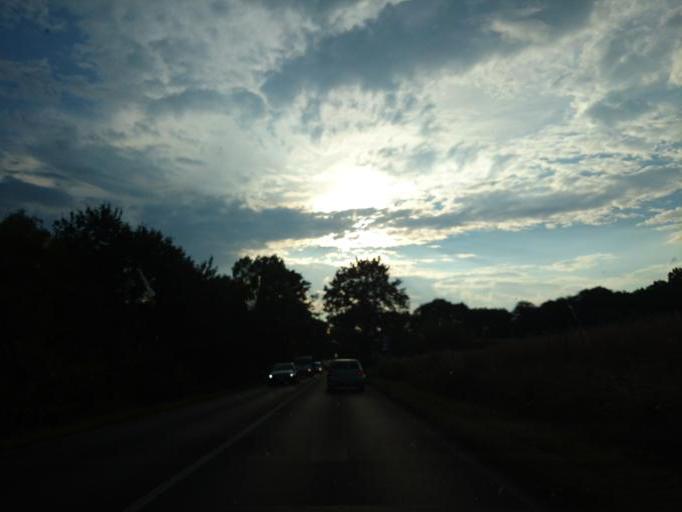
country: DE
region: Berlin
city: Hellersdorf
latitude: 52.5460
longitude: 13.6089
